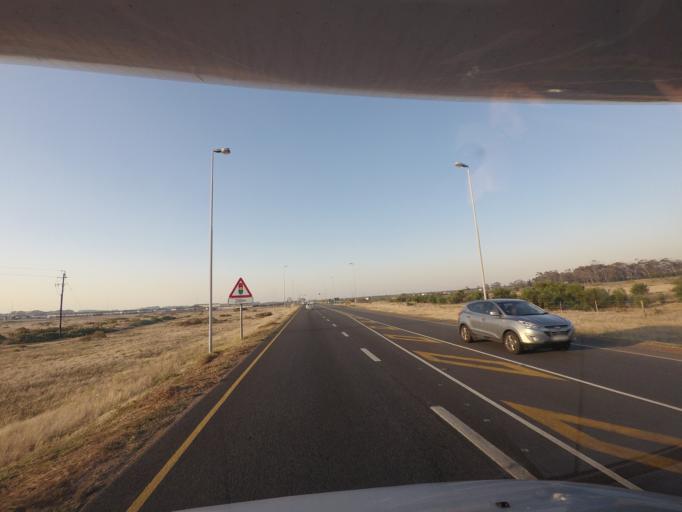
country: ZA
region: Western Cape
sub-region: City of Cape Town
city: Sunset Beach
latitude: -33.7282
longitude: 18.4555
